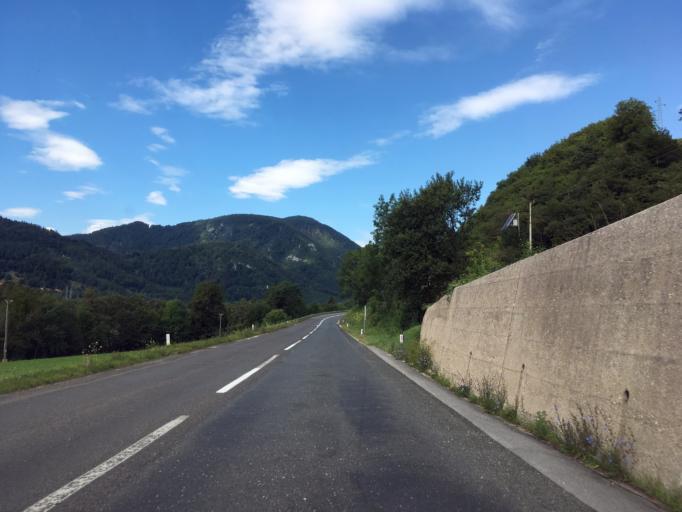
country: SI
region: Bled
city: Zasip
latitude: 46.4164
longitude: 14.1135
